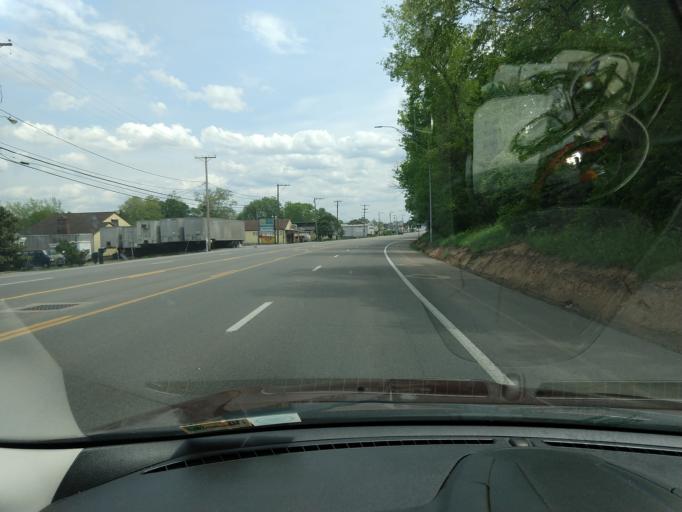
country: US
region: West Virginia
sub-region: Kanawha County
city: Dunbar
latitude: 38.3726
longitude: -81.7726
